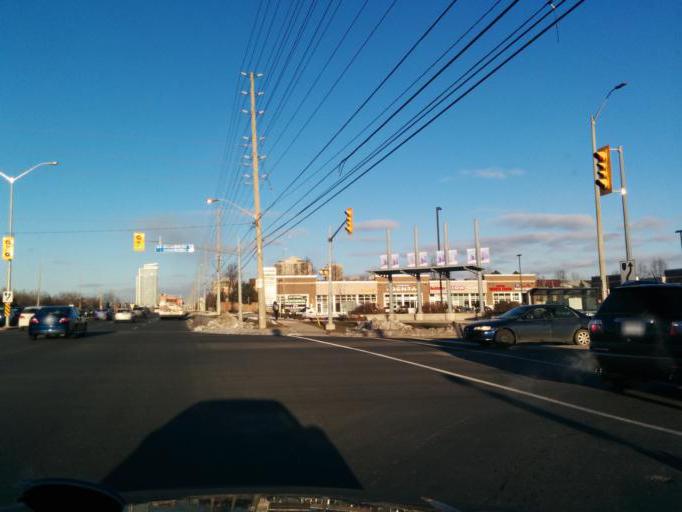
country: CA
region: Ontario
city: Mississauga
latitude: 43.5970
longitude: -79.6637
